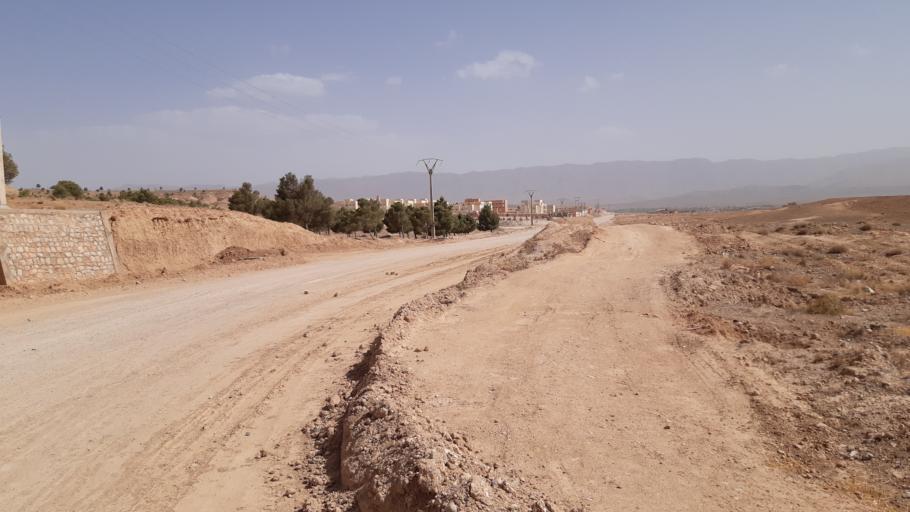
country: MA
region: Meknes-Tafilalet
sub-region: Khenifra
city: Midelt
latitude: 32.7000
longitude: -4.7631
